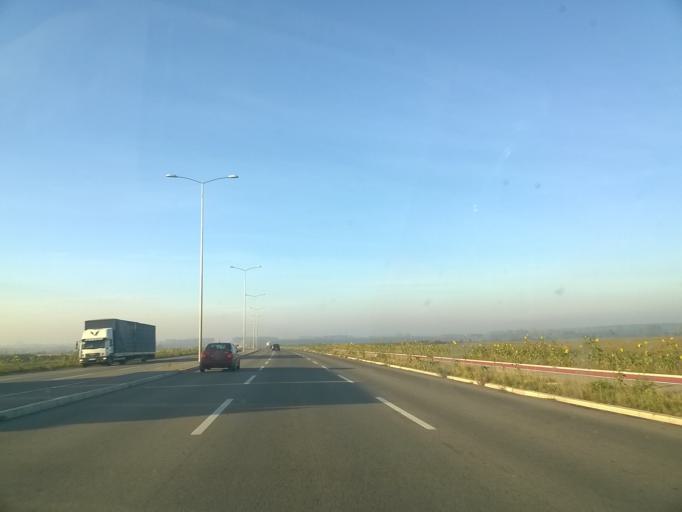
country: RS
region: Central Serbia
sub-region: Belgrade
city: Zemun
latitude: 44.8852
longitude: 20.4004
